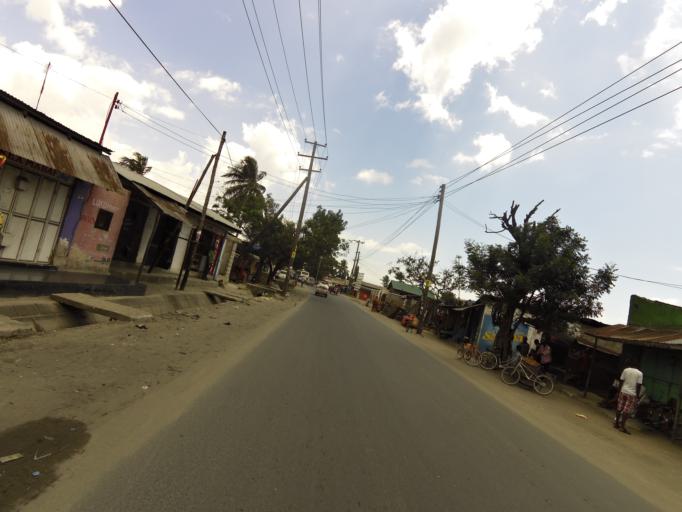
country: TZ
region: Dar es Salaam
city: Magomeni
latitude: -6.7930
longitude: 39.2460
